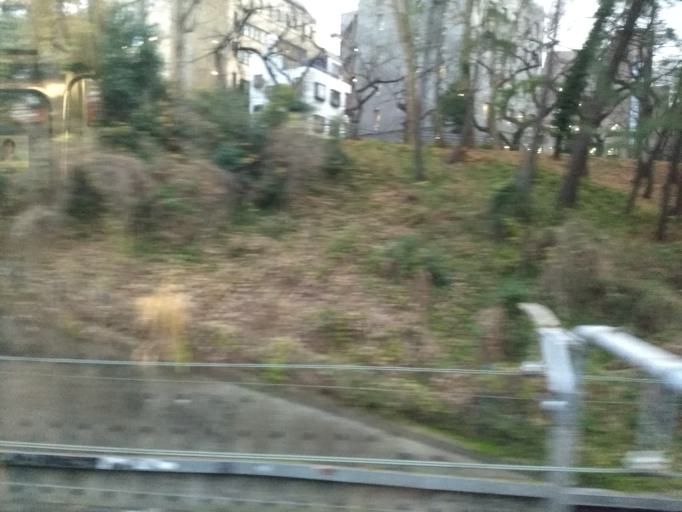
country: JP
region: Tokyo
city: Tokyo
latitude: 35.6886
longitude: 139.7316
